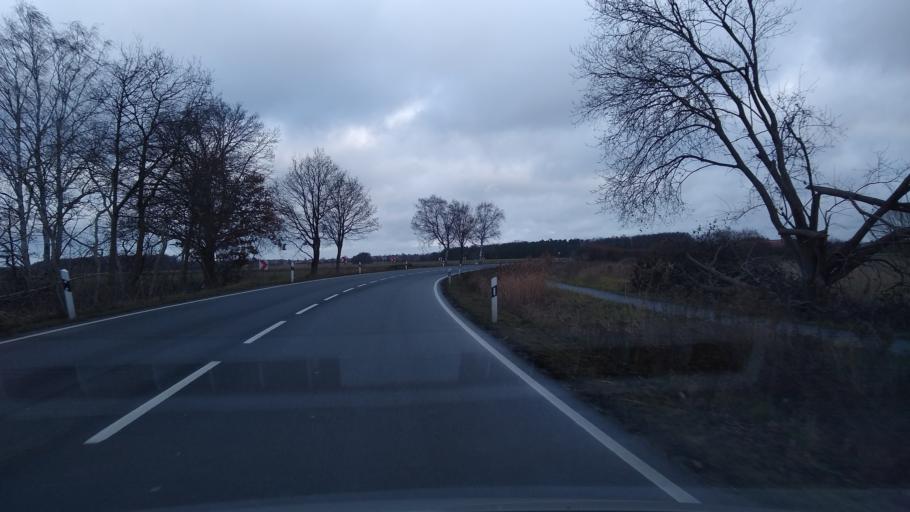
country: DE
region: Lower Saxony
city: Edemissen
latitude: 52.3724
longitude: 10.2494
